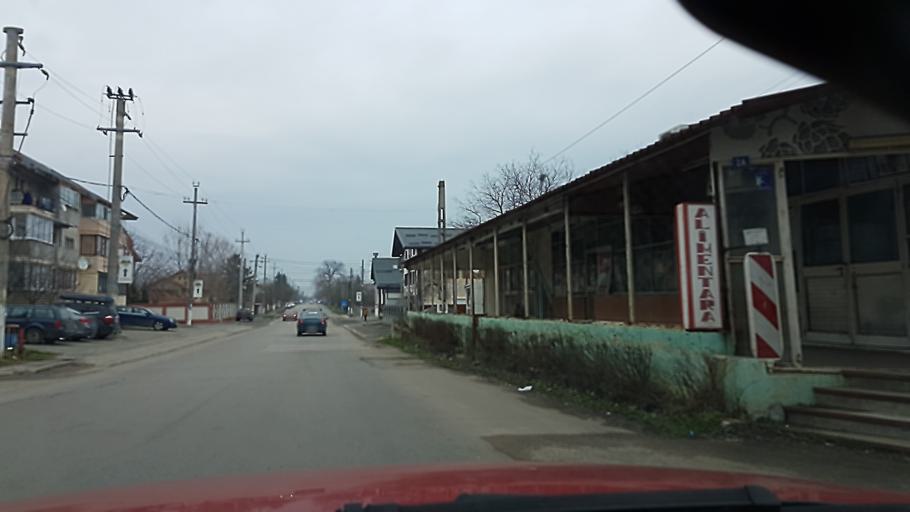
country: RO
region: Ilfov
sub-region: Comuna Balotesti
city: Balotesti
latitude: 44.6209
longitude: 26.0990
